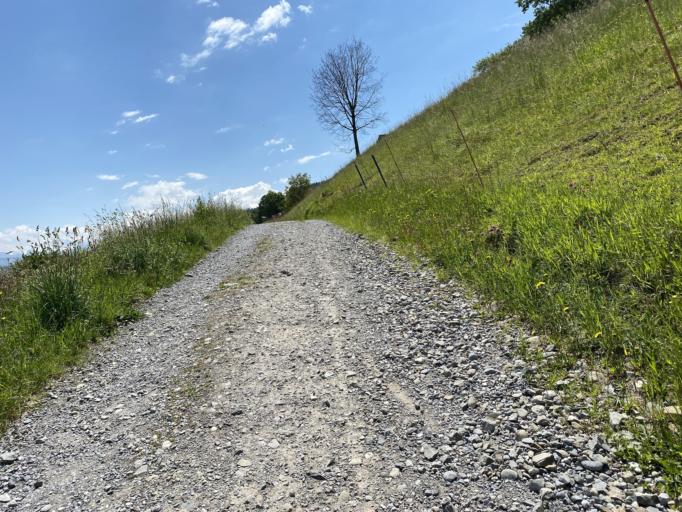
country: CH
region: Zurich
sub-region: Bezirk Horgen
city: Horgen / Scheller-Stockerstrasse
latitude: 47.2652
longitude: 8.5815
